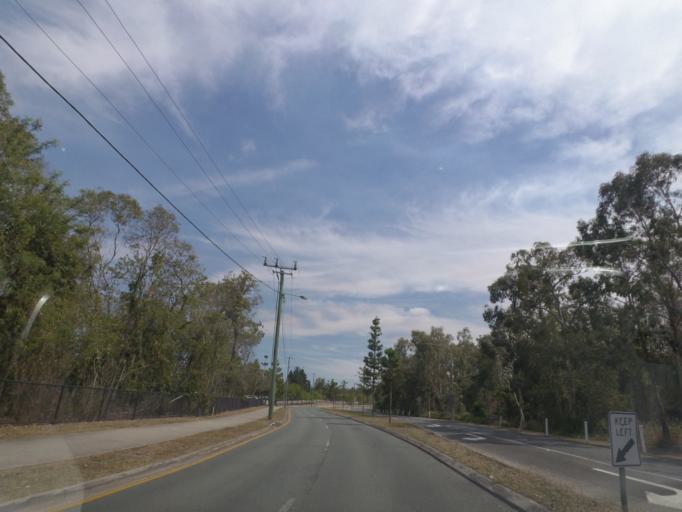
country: AU
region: Queensland
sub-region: Brisbane
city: Sunnybank Hills
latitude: -27.6357
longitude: 153.0576
